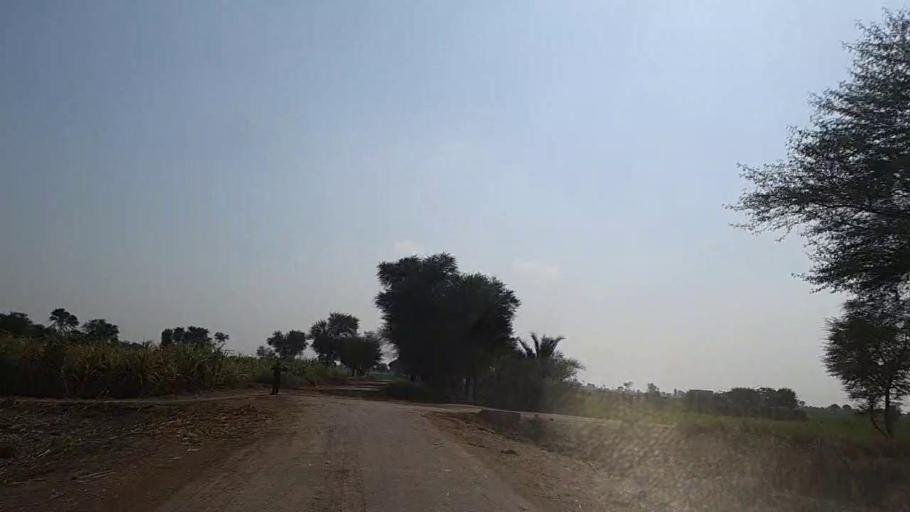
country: PK
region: Sindh
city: Daur
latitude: 26.4364
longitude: 68.2333
